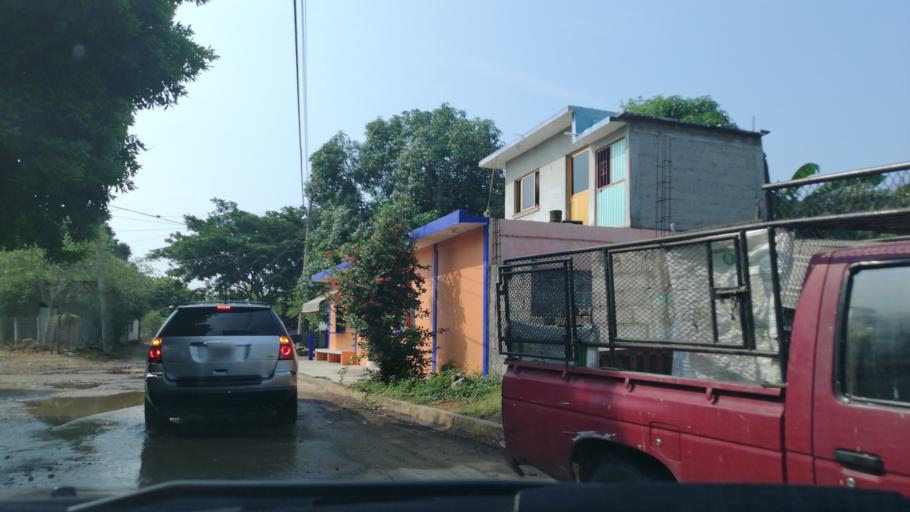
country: MX
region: Oaxaca
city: San Blas Atempa
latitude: 16.3386
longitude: -95.2201
